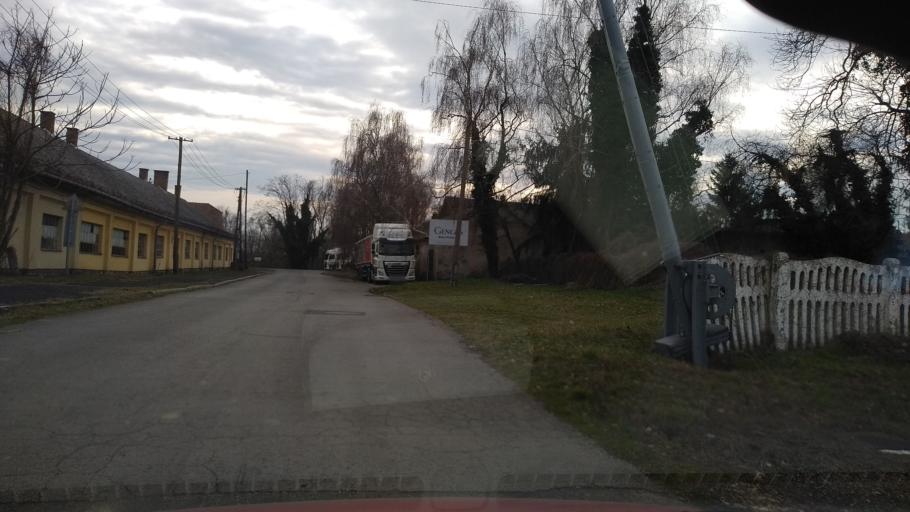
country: HU
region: Somogy
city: Barcs
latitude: 45.9525
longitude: 17.4423
